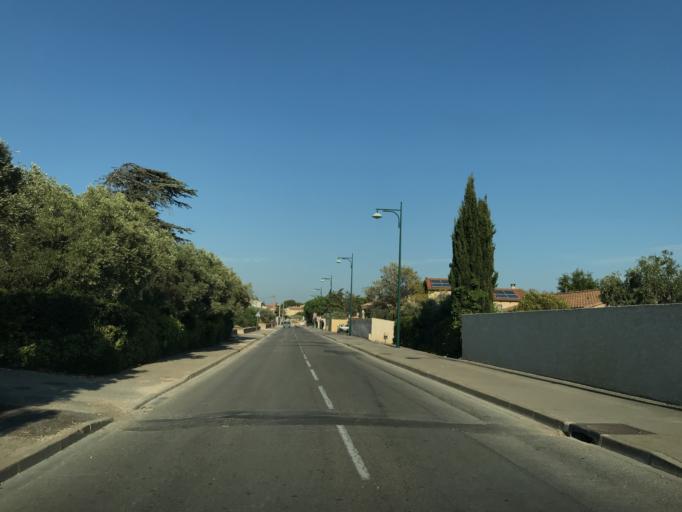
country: FR
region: Provence-Alpes-Cote d'Azur
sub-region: Departement des Bouches-du-Rhone
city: La Fare-les-Oliviers
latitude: 43.5504
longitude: 5.1860
